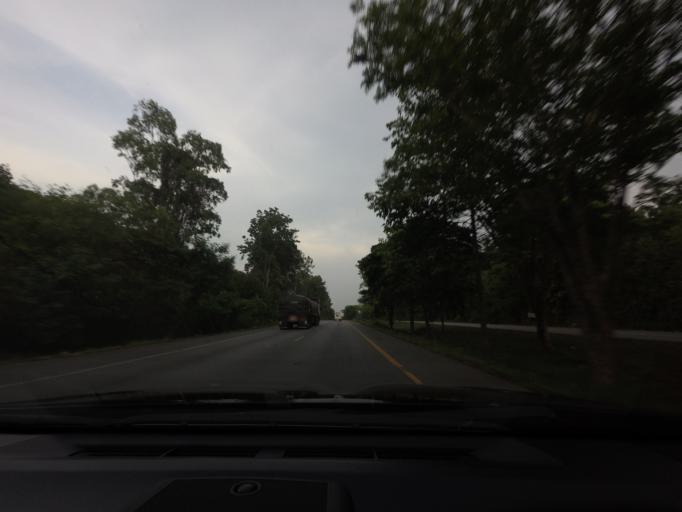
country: TH
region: Surat Thani
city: Tha Chana
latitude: 9.4738
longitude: 99.1478
